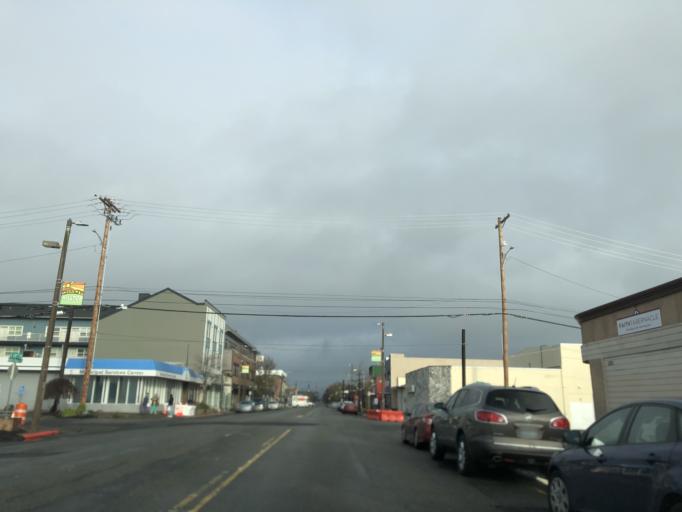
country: US
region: Washington
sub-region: Pierce County
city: Tacoma
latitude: 47.2495
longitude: -122.4511
